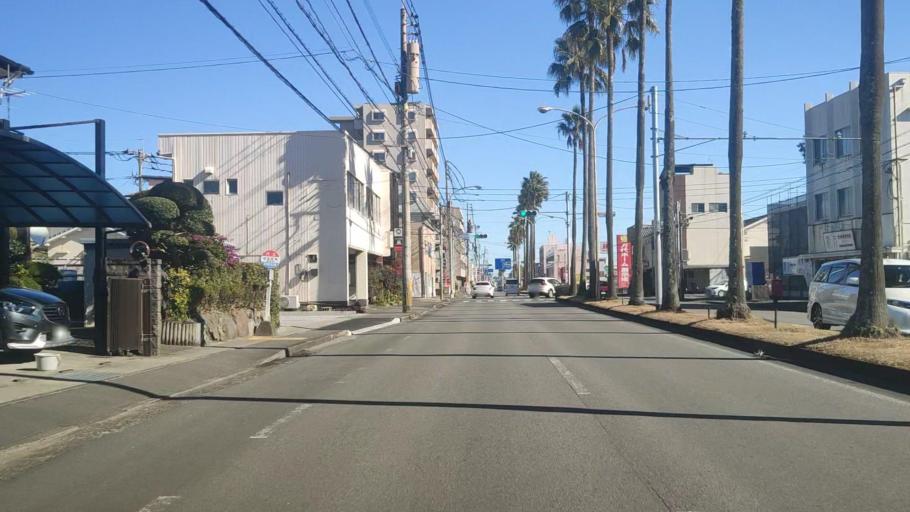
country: JP
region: Miyazaki
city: Miyazaki-shi
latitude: 31.9077
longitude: 131.4380
